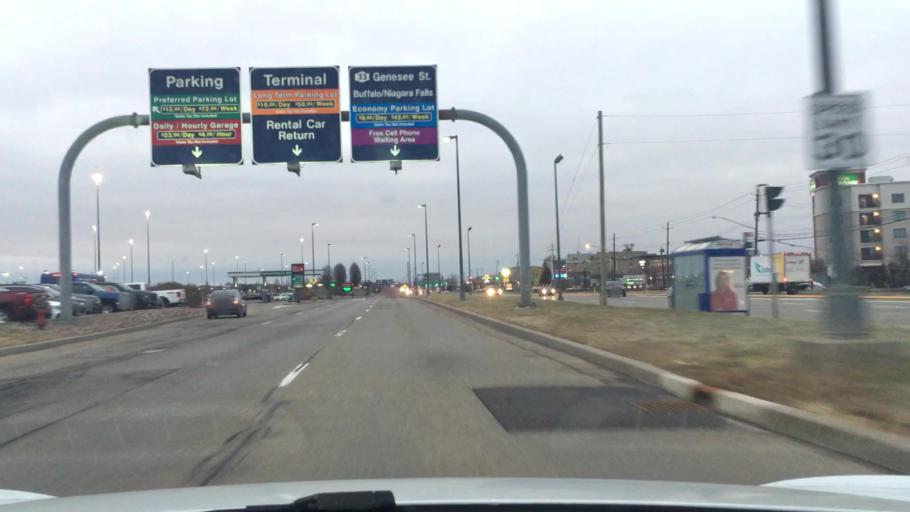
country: US
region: New York
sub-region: Erie County
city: Williamsville
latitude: 42.9319
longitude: -78.7311
